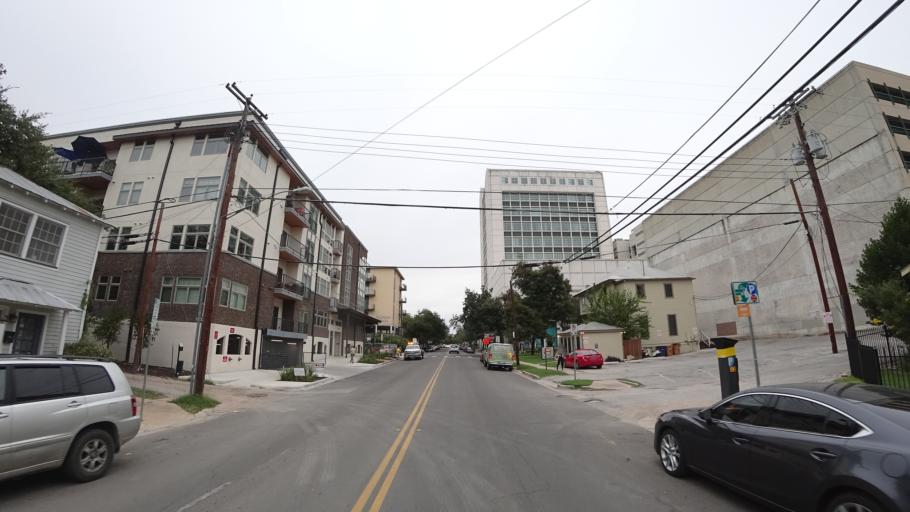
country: US
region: Texas
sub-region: Travis County
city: Austin
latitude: 30.2728
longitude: -97.7473
